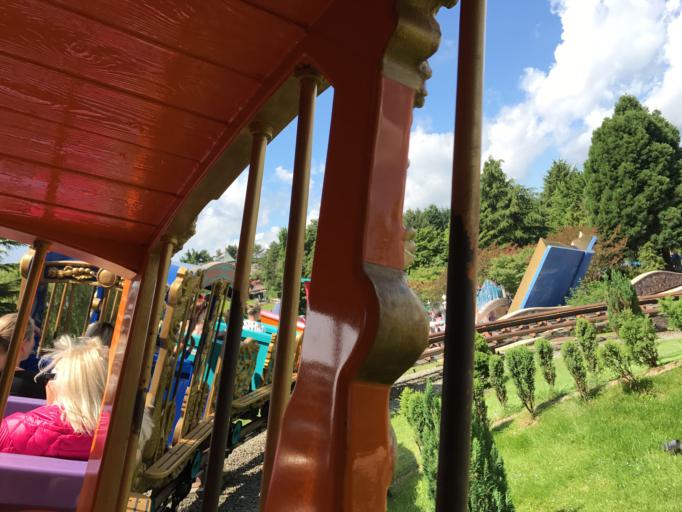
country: FR
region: Ile-de-France
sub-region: Departement de Seine-et-Marne
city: Chessy
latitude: 48.8755
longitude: 2.7753
